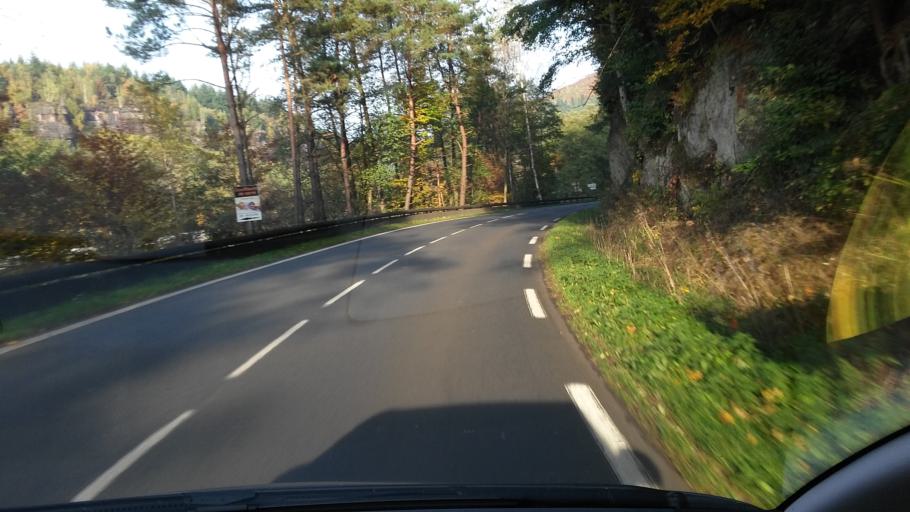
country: FR
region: Lorraine
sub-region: Departement de la Moselle
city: Phalsbourg
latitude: 48.7180
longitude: 7.2233
